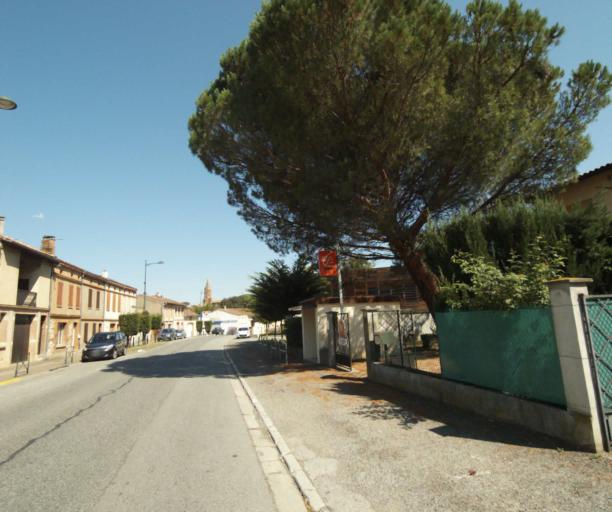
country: FR
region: Midi-Pyrenees
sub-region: Departement de l'Ariege
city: Lezat-sur-Leze
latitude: 43.2725
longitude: 1.3479
